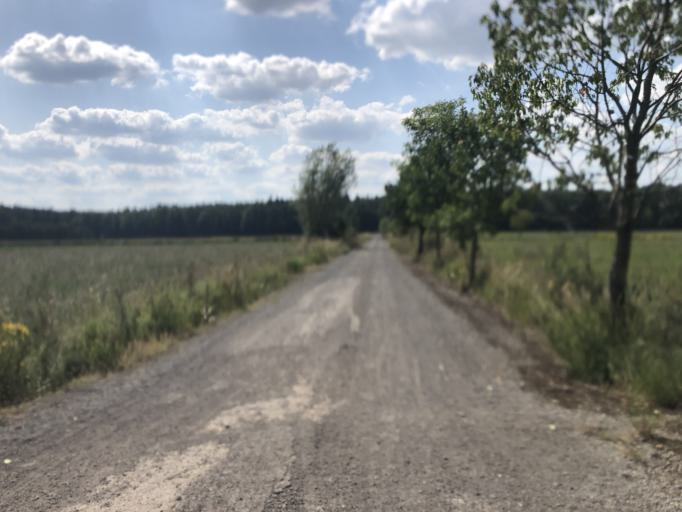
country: DE
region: Brandenburg
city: Mullrose
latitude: 52.2328
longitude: 14.3978
